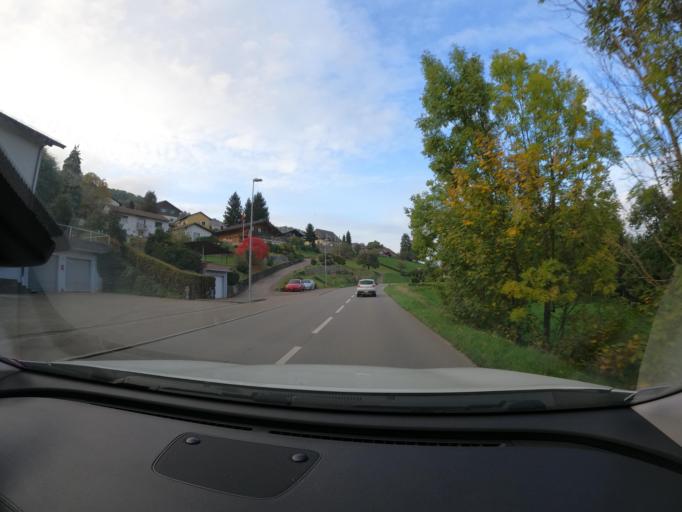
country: CH
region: Bern
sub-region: Bern-Mittelland District
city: Toffen
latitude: 46.8695
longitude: 7.4913
